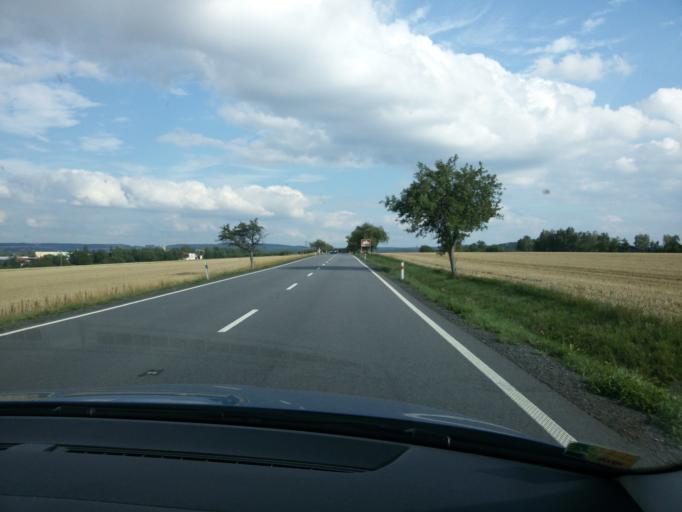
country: CZ
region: Pardubicky
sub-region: Okres Svitavy
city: Policka
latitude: 49.7188
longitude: 16.2420
